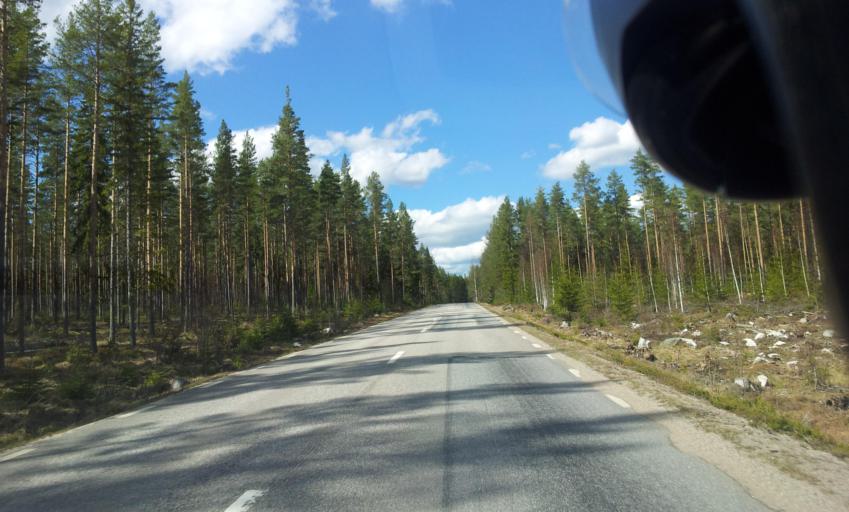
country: SE
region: Gaevleborg
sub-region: Ovanakers Kommun
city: Edsbyn
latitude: 61.3358
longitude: 15.8280
